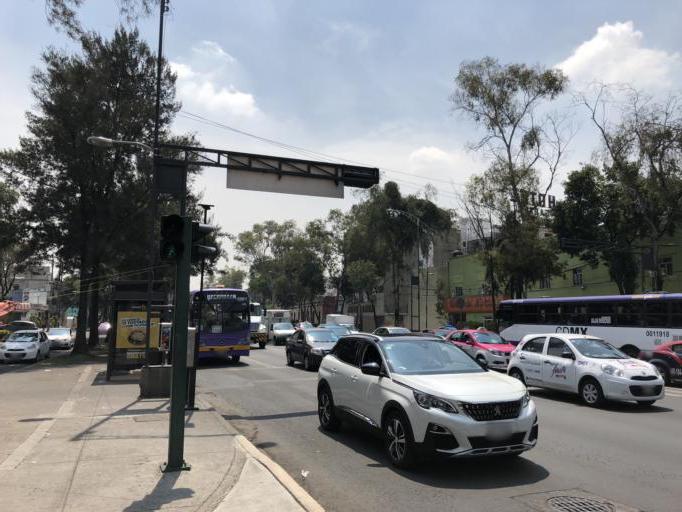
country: MX
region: Mexico City
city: Cuauhtemoc
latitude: 19.4531
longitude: -99.1296
